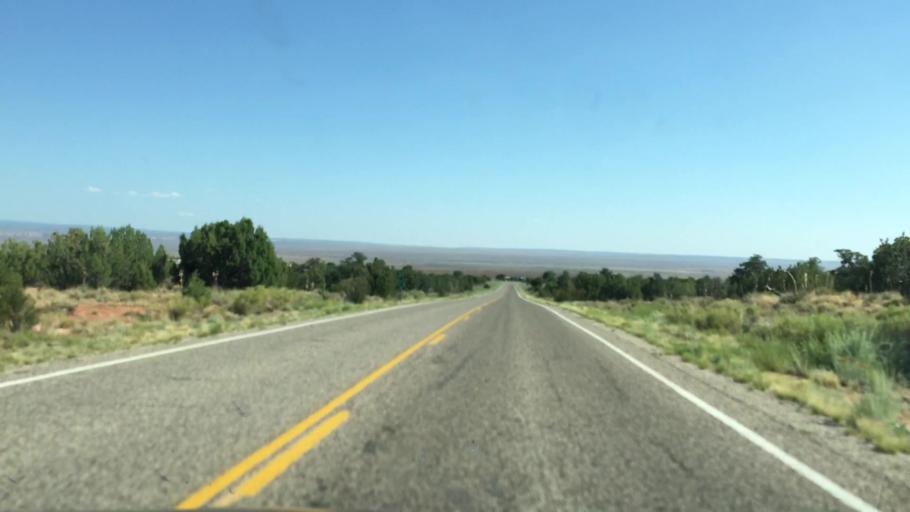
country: US
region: Arizona
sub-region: Coconino County
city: Fredonia
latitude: 36.8722
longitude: -112.7381
